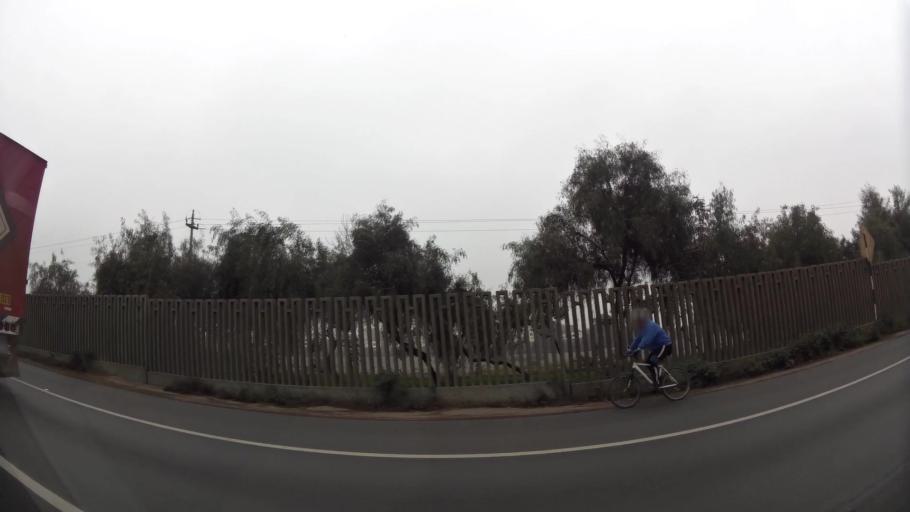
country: PE
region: Lima
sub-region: Lima
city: Vitarte
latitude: -12.0214
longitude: -76.9276
